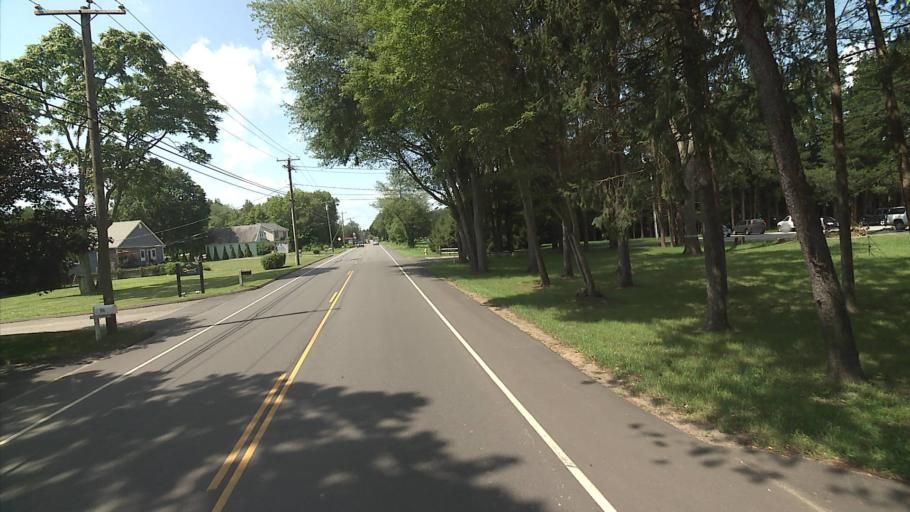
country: US
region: Connecticut
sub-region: Middlesex County
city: Essex Village
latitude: 41.3450
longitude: -72.4093
